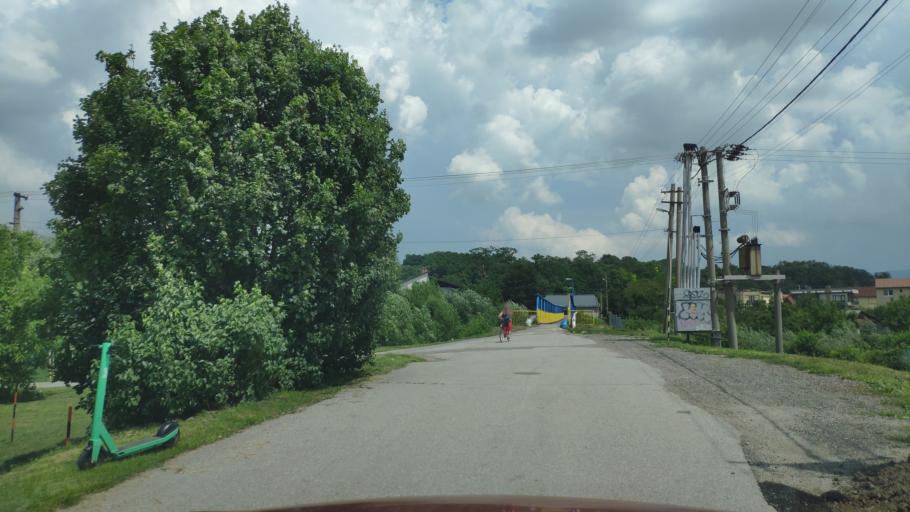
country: SK
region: Kosicky
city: Kosice
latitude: 48.6727
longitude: 21.3091
